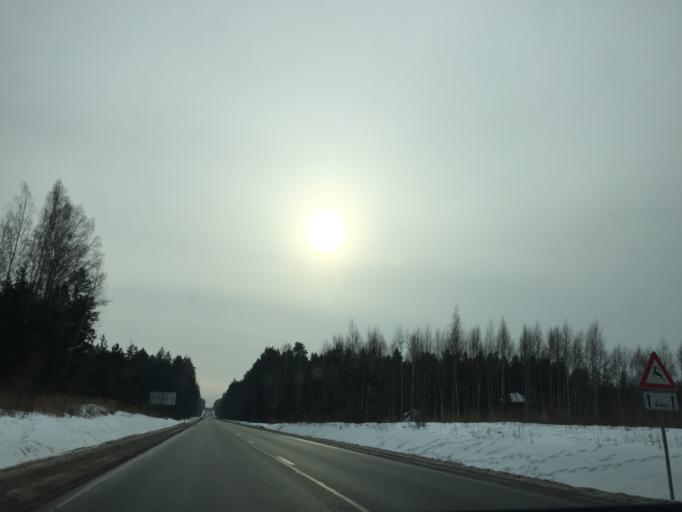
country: LV
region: Ogre
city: Ogre
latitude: 56.8566
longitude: 24.5660
